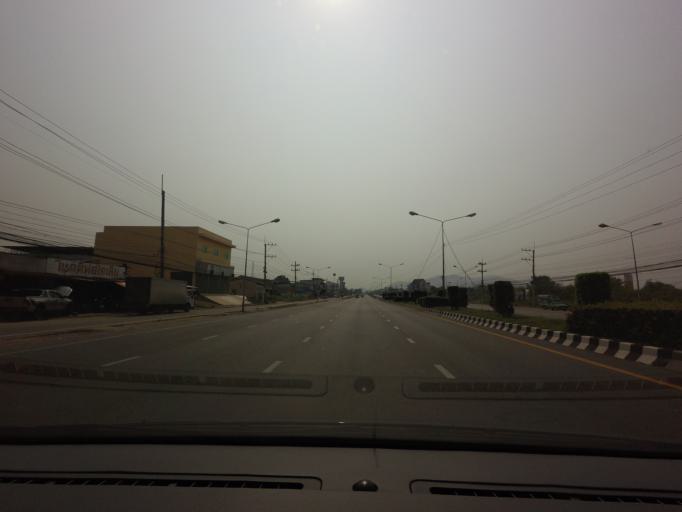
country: TH
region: Prachuap Khiri Khan
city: Pran Buri
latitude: 12.3815
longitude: 99.8940
